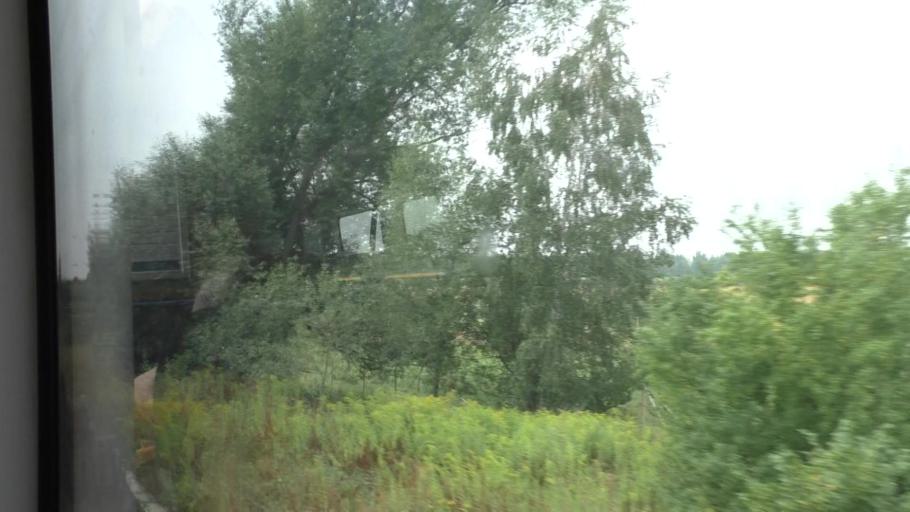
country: DE
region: Saxony
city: Hirschfelde
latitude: 50.9354
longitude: 14.8763
